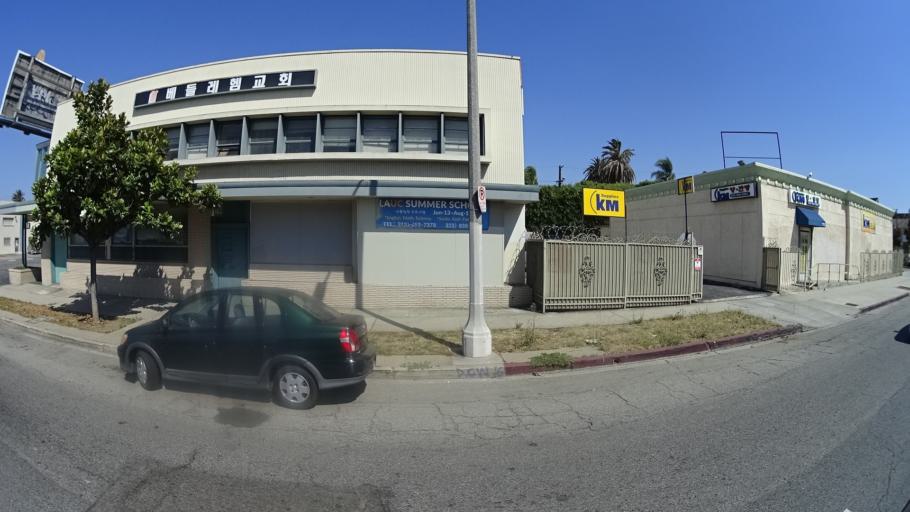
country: US
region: California
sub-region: Los Angeles County
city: Hollywood
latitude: 34.0519
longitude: -118.3246
